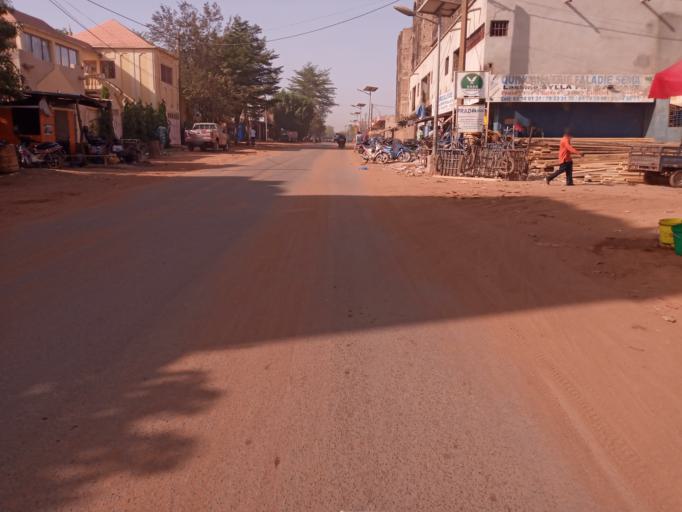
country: ML
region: Bamako
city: Bamako
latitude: 12.5841
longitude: -7.9529
